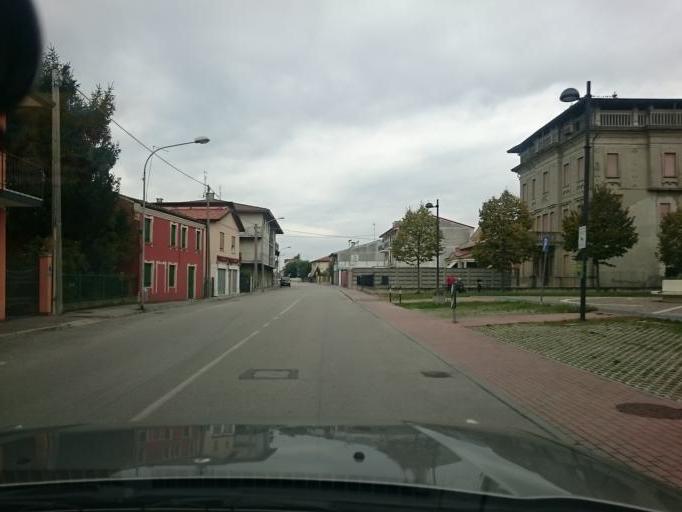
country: IT
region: Veneto
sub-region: Provincia di Padova
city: Arzergrande
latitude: 45.2733
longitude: 12.0498
